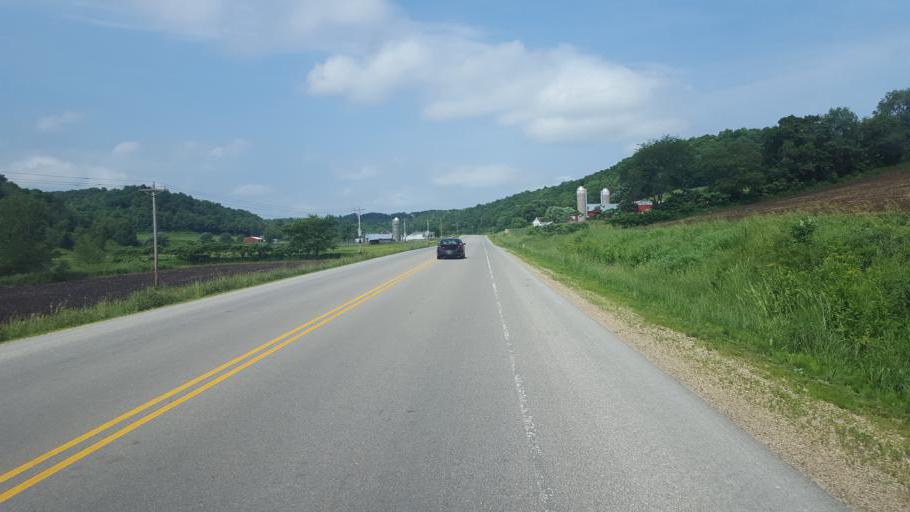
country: US
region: Wisconsin
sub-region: Monroe County
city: Cashton
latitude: 43.7335
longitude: -90.6890
